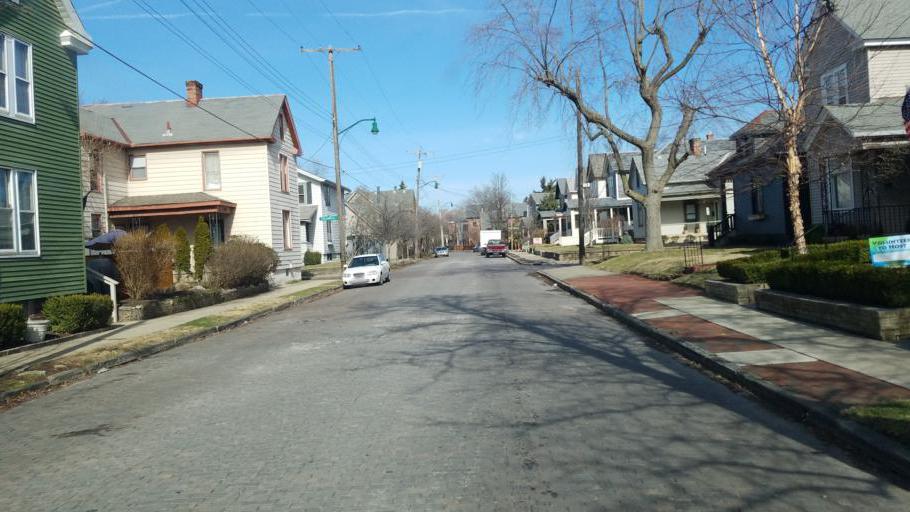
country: US
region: Ohio
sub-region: Franklin County
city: Columbus
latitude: 39.9465
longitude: -82.9898
